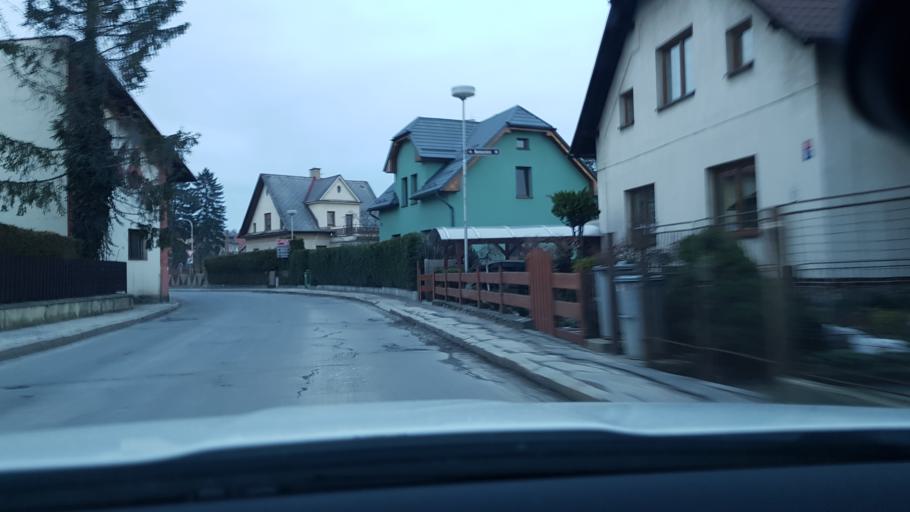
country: CZ
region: Olomoucky
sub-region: Okres Jesenik
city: Jesenik
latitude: 50.2257
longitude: 17.1926
